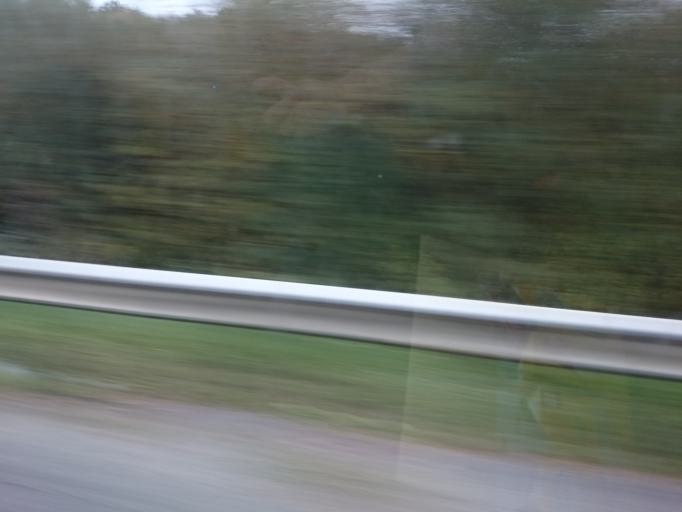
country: FR
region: Pays de la Loire
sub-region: Departement de la Loire-Atlantique
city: Saint-Herblain
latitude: 47.2416
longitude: -1.6380
